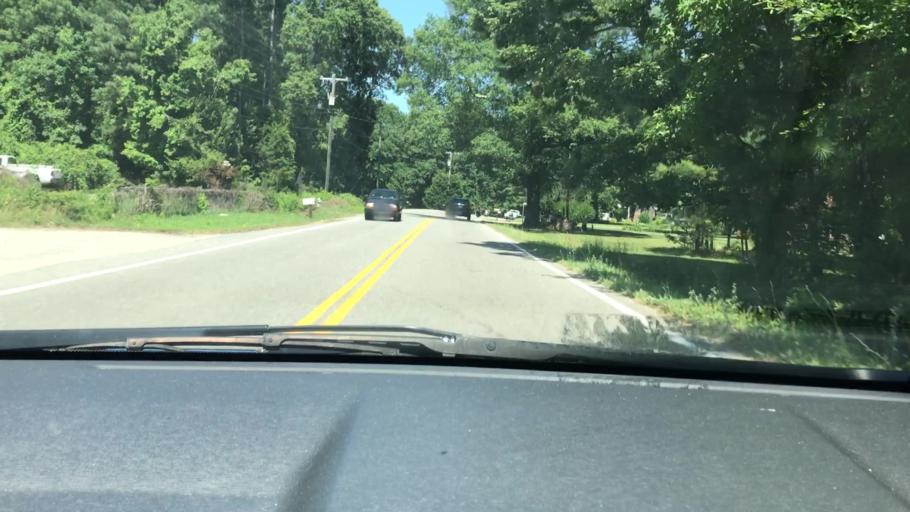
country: US
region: Virginia
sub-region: Hanover County
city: Ashland
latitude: 37.7155
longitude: -77.4648
